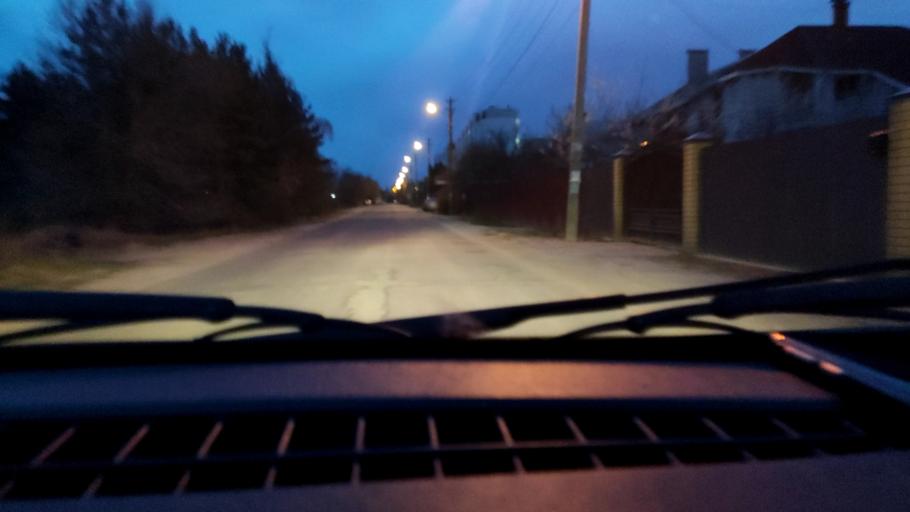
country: RU
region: Voronezj
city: Somovo
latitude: 51.7395
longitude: 39.2962
